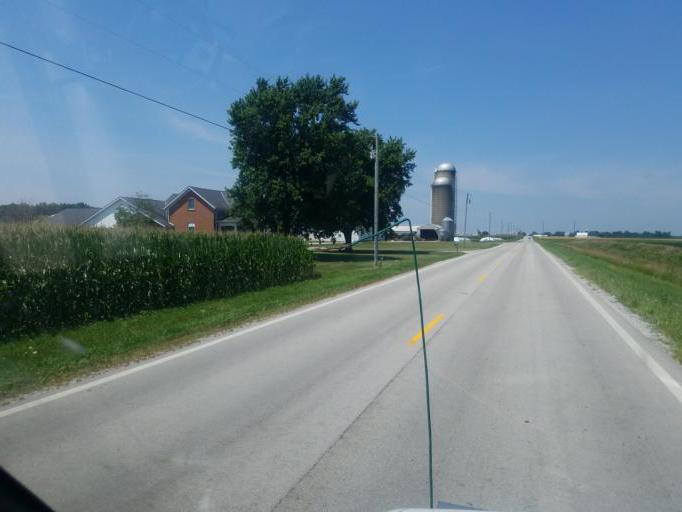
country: US
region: Ohio
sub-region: Auglaize County
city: Minster
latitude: 40.3719
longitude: -84.4341
